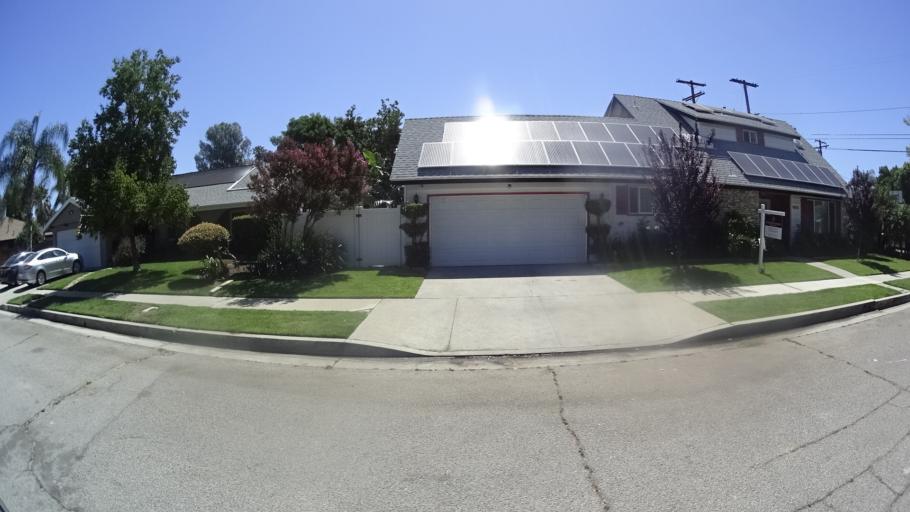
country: US
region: California
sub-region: Los Angeles County
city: Van Nuys
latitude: 34.1966
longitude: -118.4957
